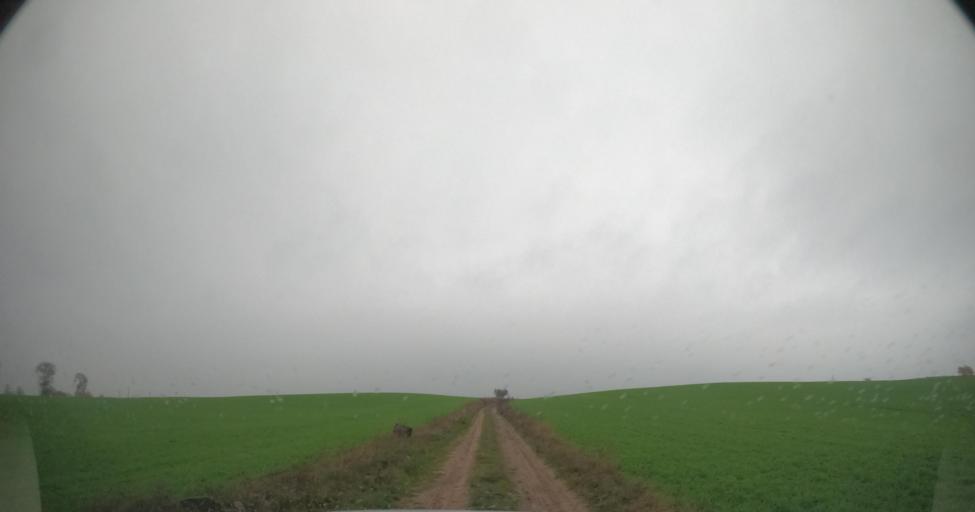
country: PL
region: West Pomeranian Voivodeship
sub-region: Powiat drawski
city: Drawsko Pomorskie
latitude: 53.5248
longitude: 15.7812
